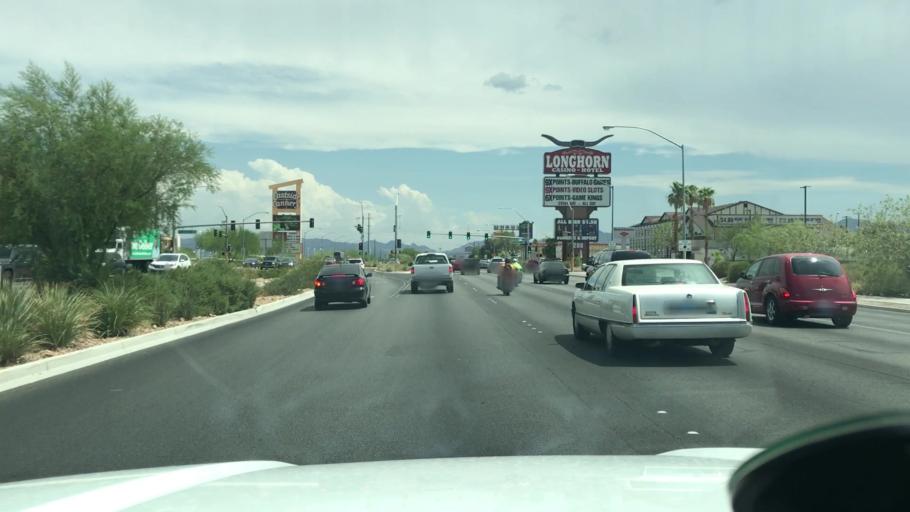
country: US
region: Nevada
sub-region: Clark County
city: Whitney
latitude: 36.1090
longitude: -115.0602
